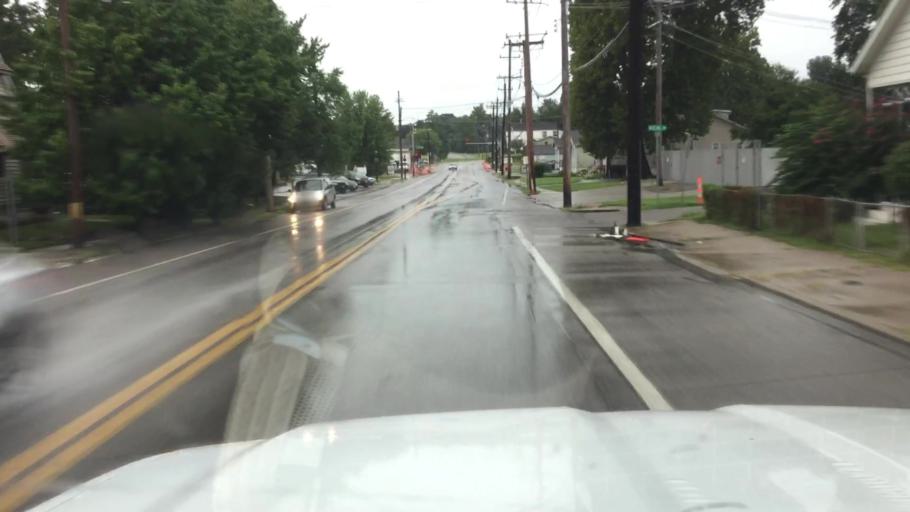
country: US
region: Missouri
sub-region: Saint Louis County
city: Lemay
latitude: 38.5261
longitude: -90.2773
